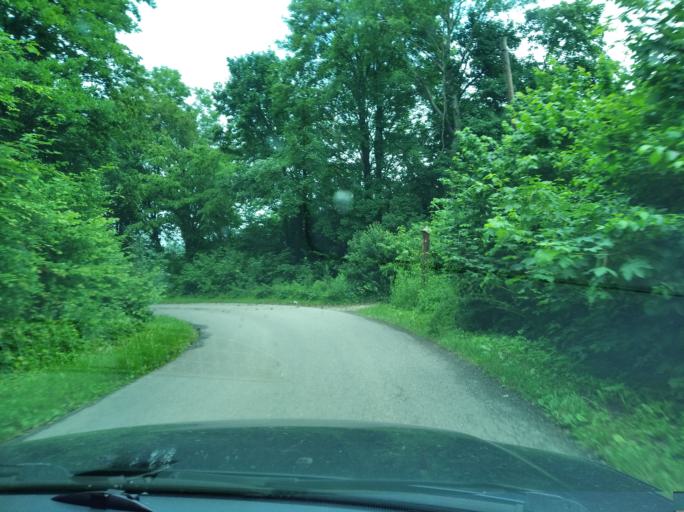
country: PL
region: Subcarpathian Voivodeship
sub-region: Powiat jaroslawski
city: Pruchnik
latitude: 49.8934
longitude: 22.5267
